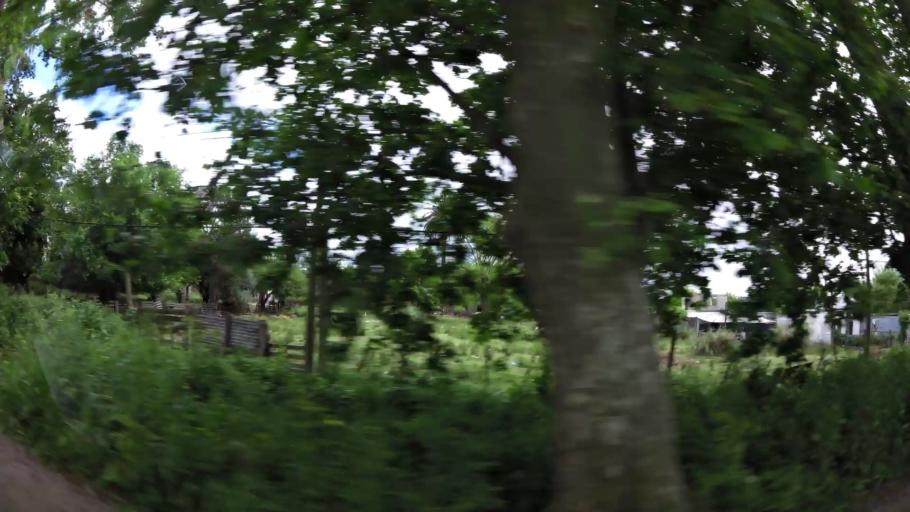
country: UY
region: Canelones
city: La Paz
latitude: -34.8043
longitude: -56.1598
